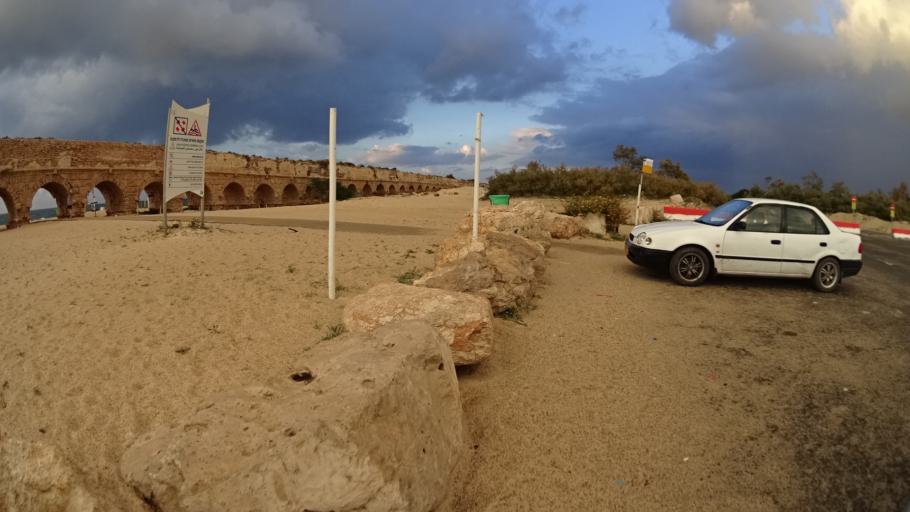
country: IL
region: Haifa
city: Qesarya
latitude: 32.5126
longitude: 34.8970
